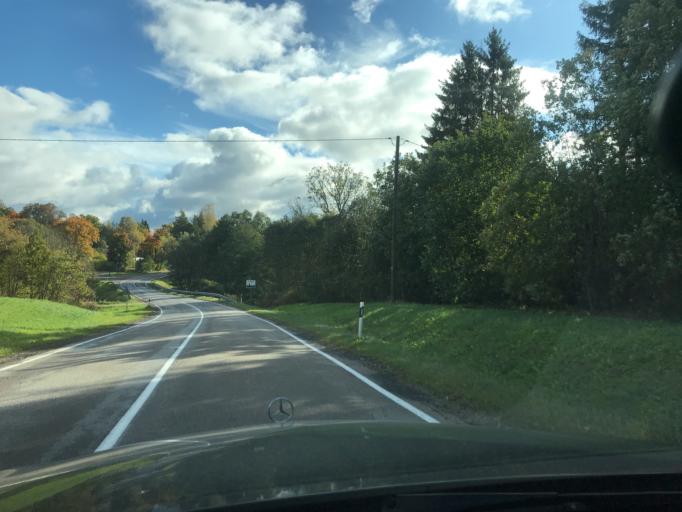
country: EE
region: Valgamaa
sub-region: Torva linn
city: Torva
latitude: 58.0091
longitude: 26.1982
